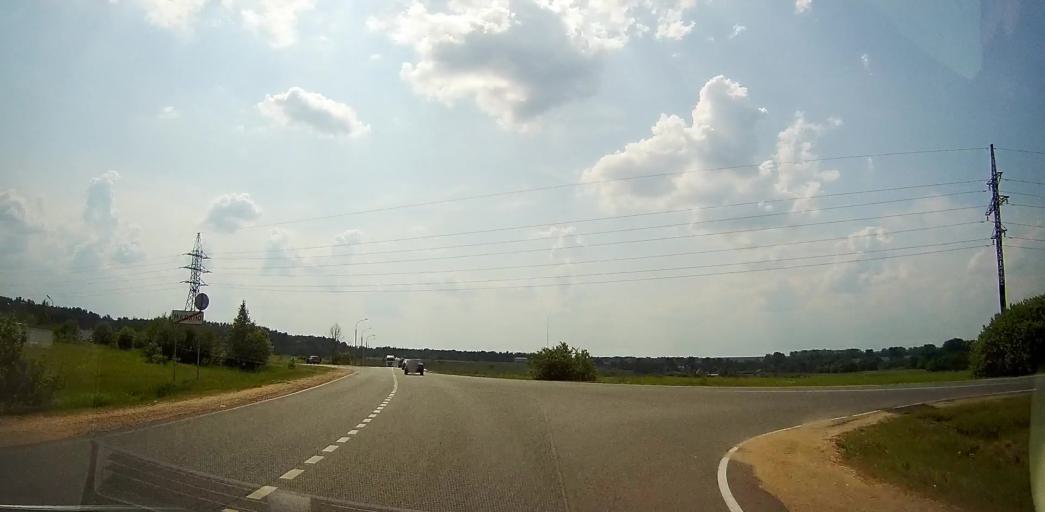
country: RU
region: Moskovskaya
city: Malino
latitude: 55.1021
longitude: 38.1712
